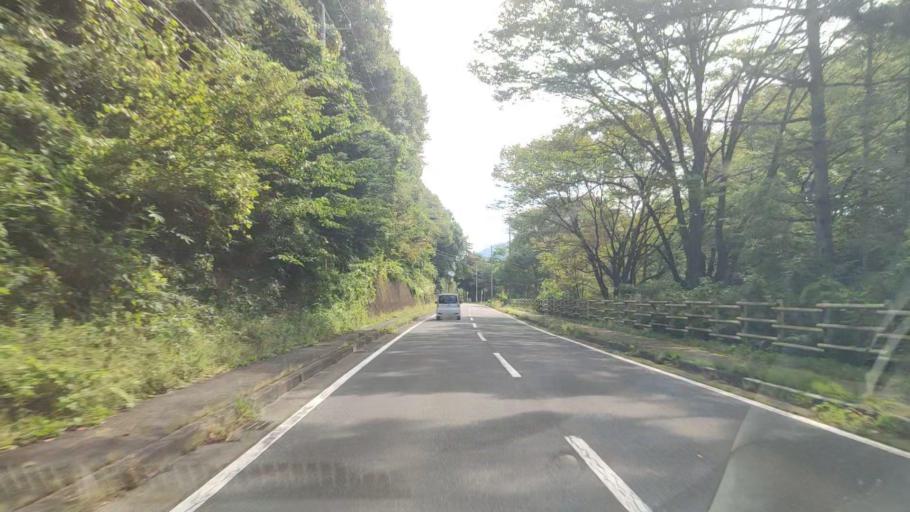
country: JP
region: Gunma
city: Nakanojomachi
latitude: 36.6211
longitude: 138.9321
